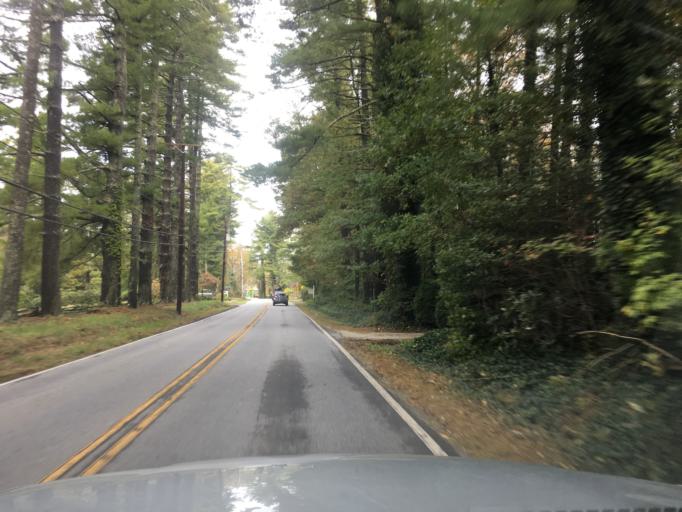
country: US
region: North Carolina
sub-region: Henderson County
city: Flat Rock
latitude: 35.2677
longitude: -82.4393
